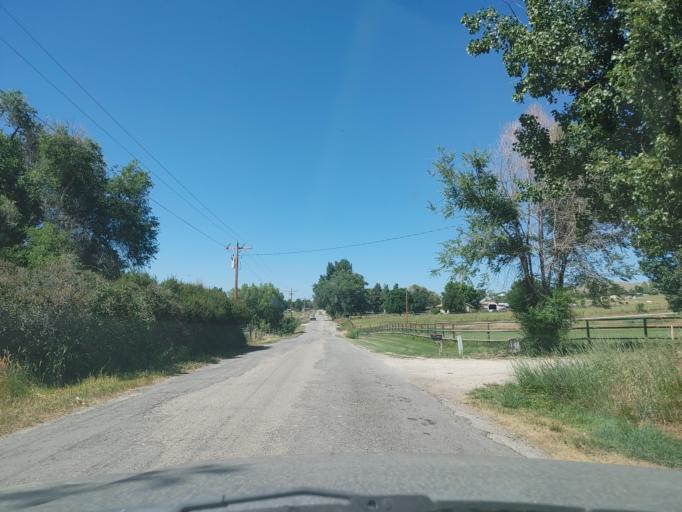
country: US
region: Montana
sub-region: Ravalli County
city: Hamilton
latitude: 46.3333
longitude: -114.0614
